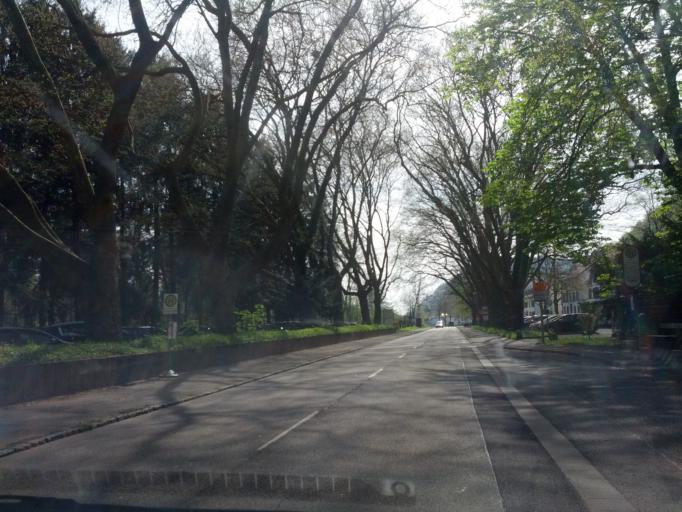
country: DE
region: Baden-Wuerttemberg
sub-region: Freiburg Region
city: Gutach im Breisgau
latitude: 48.1124
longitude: 7.9830
